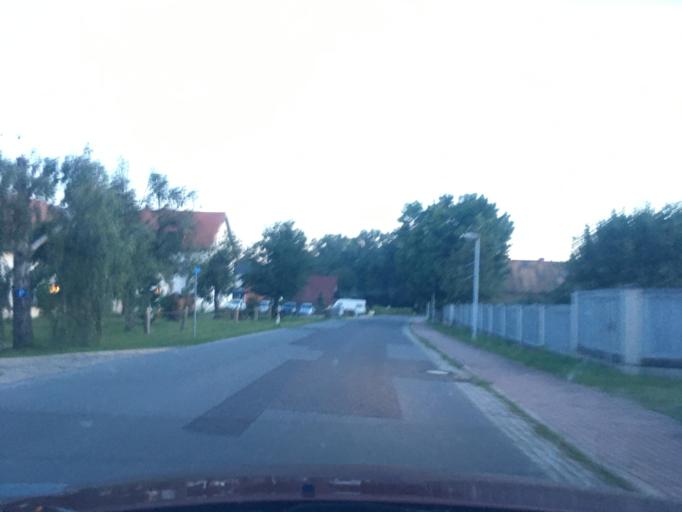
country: PL
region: Lower Silesian Voivodeship
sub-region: Powiat zgorzelecki
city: Piensk
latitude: 51.2277
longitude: 15.0080
